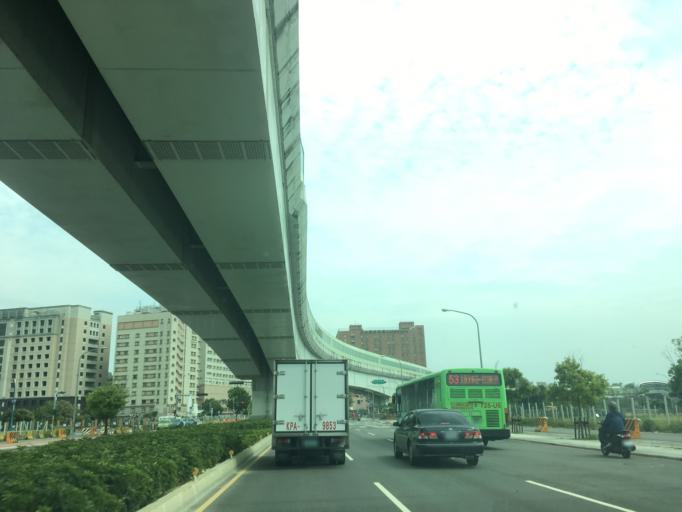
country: TW
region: Taiwan
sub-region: Taichung City
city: Taichung
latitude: 24.1242
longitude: 120.6474
